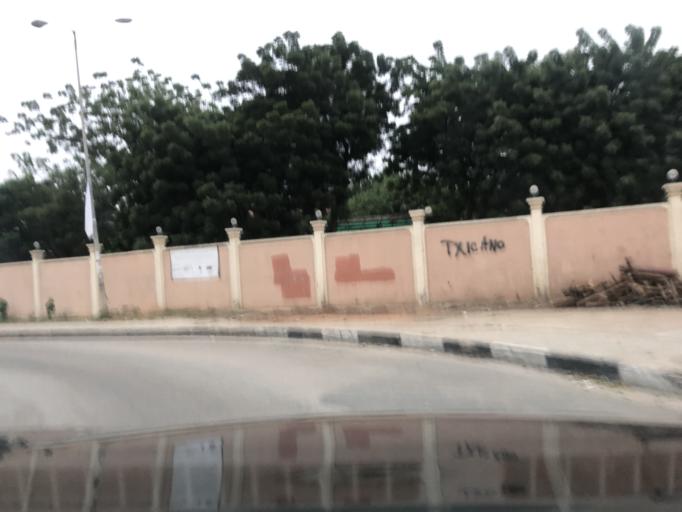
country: AO
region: Luanda
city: Luanda
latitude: -8.8298
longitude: 13.2568
